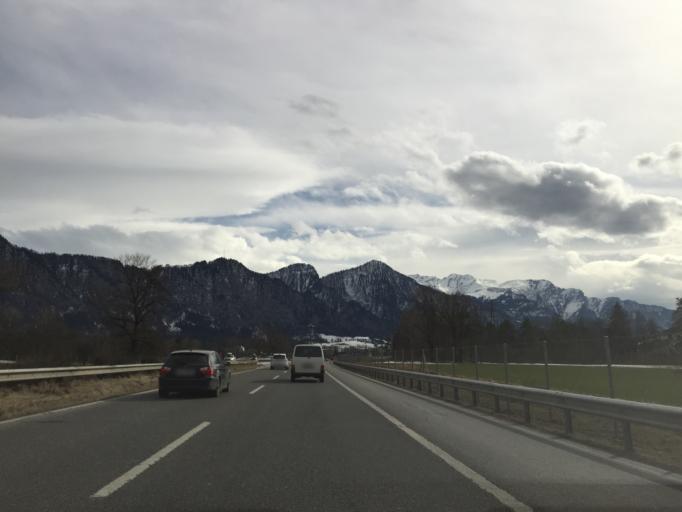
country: CH
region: Grisons
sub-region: Landquart District
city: Malans
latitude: 46.9787
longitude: 9.5470
